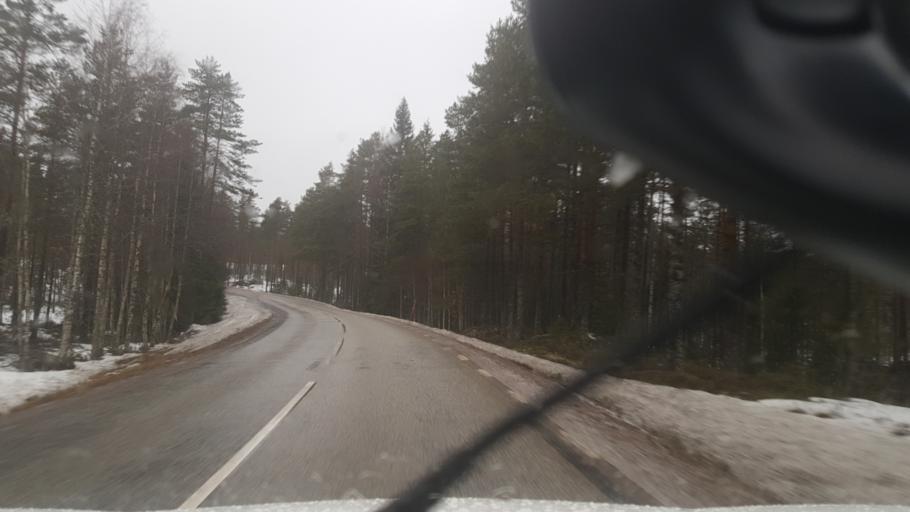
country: SE
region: Vaermland
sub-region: Arjangs Kommun
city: Arjaeng
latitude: 59.5651
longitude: 12.1907
